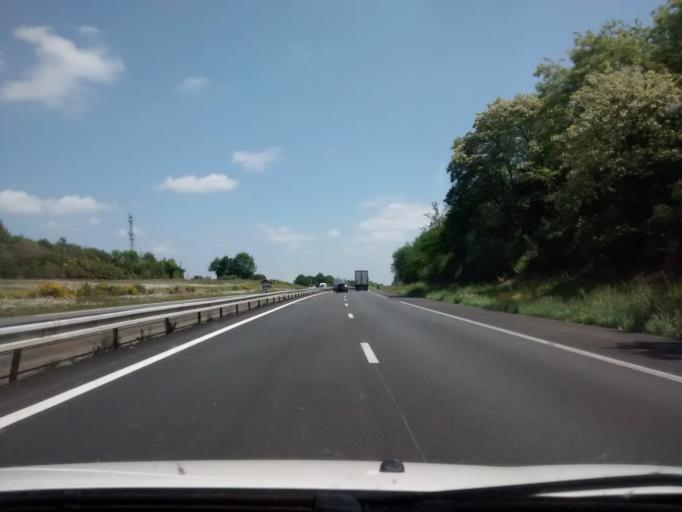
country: FR
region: Pays de la Loire
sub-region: Departement de la Sarthe
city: Brulon
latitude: 48.0111
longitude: -0.2359
